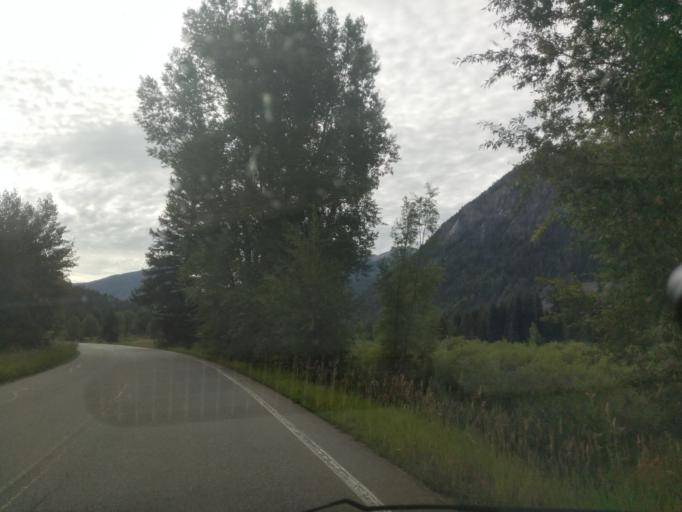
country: US
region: Colorado
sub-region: Gunnison County
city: Crested Butte
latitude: 39.0757
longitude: -107.2173
